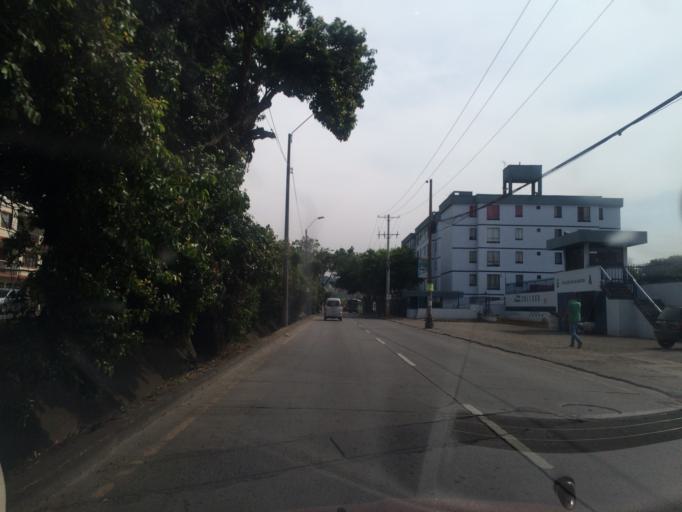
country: CO
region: Valle del Cauca
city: Cali
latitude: 3.4142
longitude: -76.5552
